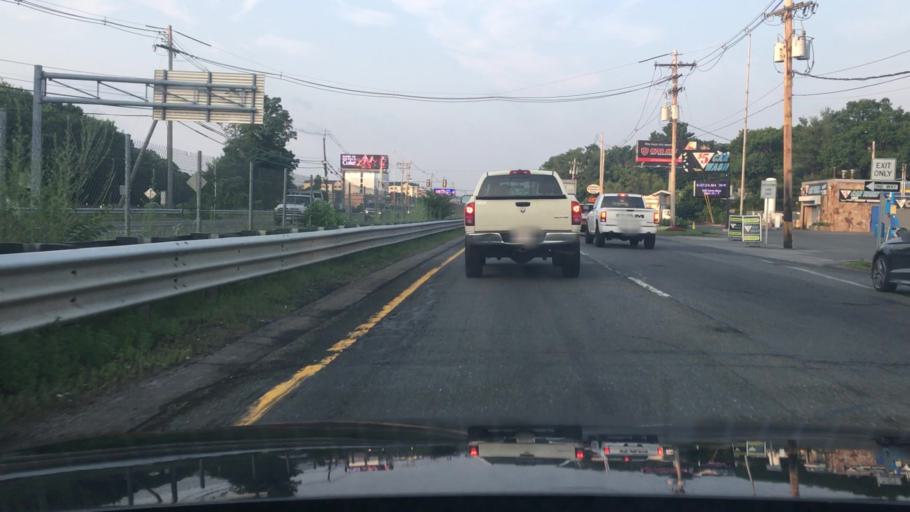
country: US
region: Massachusetts
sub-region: Essex County
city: South Peabody
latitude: 42.5306
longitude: -70.9924
